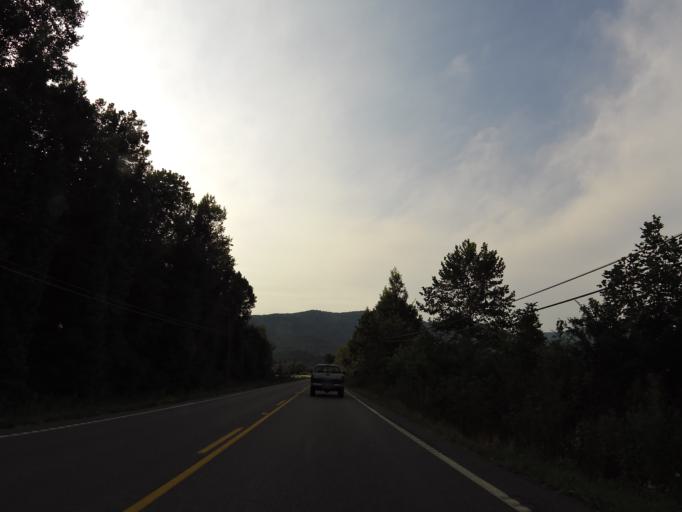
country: US
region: Tennessee
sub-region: Morgan County
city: Coalfield
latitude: 36.0653
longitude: -84.4515
